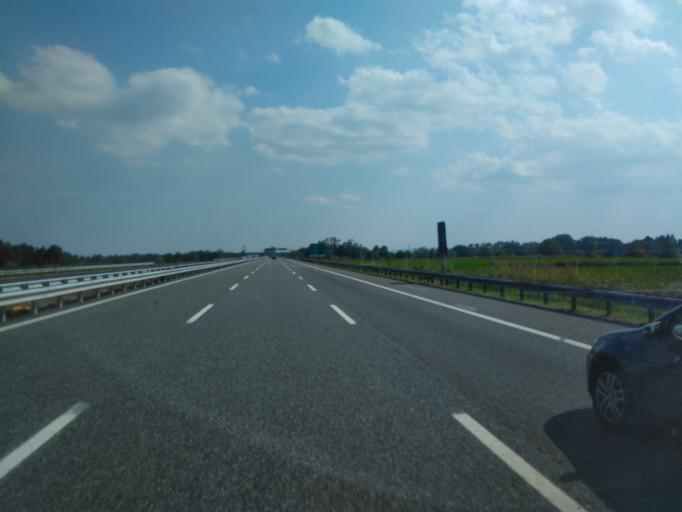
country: IT
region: Piedmont
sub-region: Provincia di Vercelli
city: Pezzana
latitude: 45.2546
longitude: 8.4671
